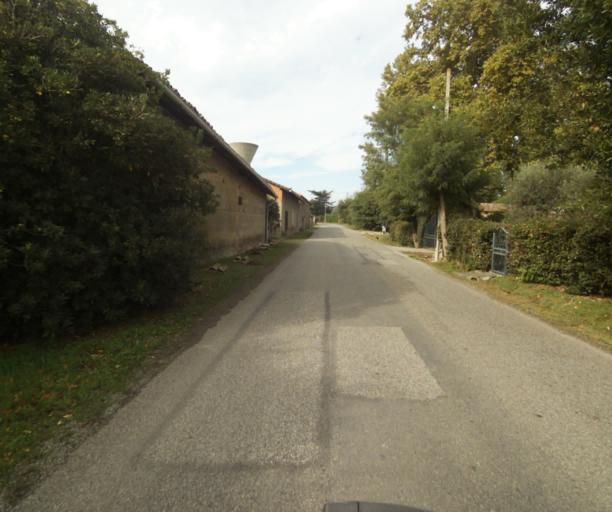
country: FR
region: Midi-Pyrenees
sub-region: Departement du Tarn-et-Garonne
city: Finhan
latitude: 43.9144
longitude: 1.2287
